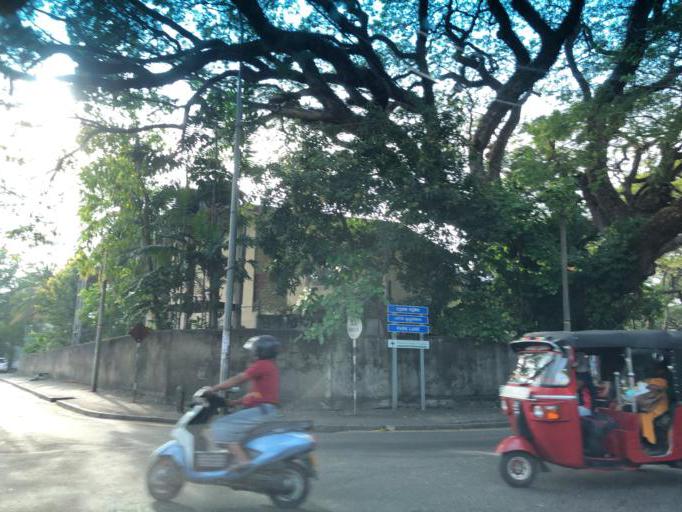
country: LK
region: Western
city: Pita Kotte
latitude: 6.8864
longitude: 79.8690
